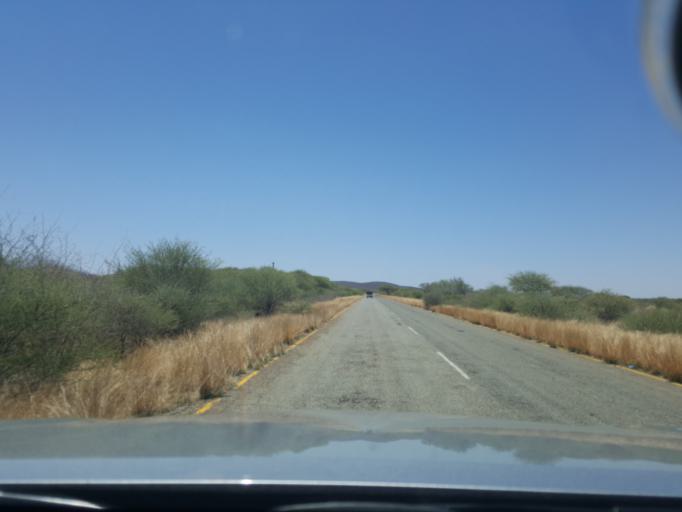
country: BW
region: South East
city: Ramotswa
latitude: -25.0879
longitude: 25.9577
